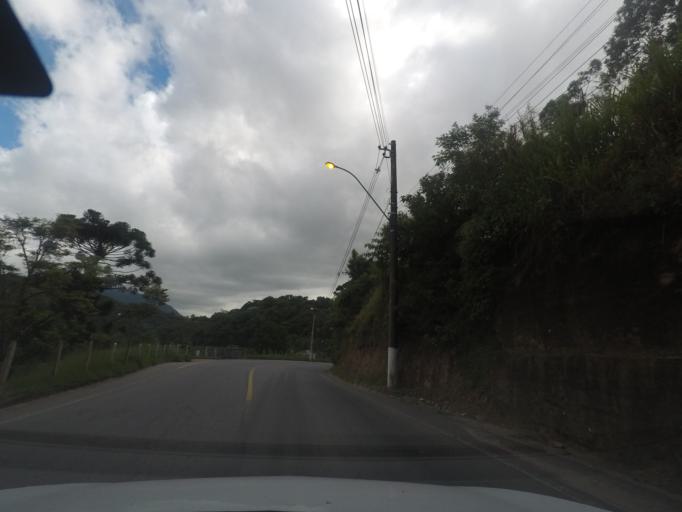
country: BR
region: Rio de Janeiro
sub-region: Teresopolis
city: Teresopolis
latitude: -22.3946
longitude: -42.9578
